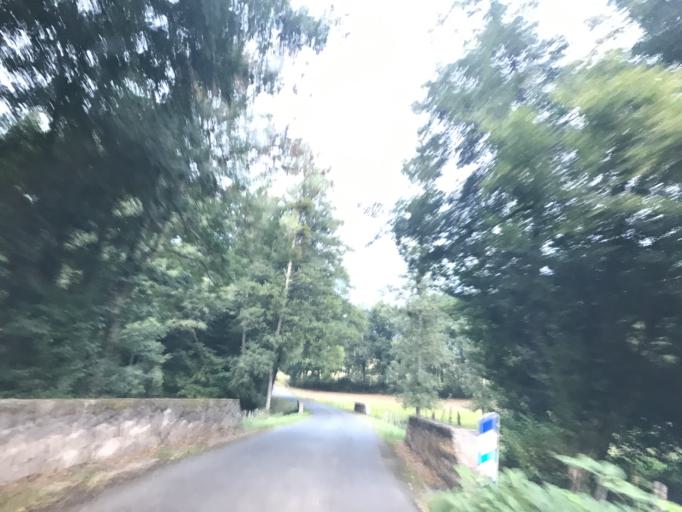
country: FR
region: Auvergne
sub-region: Departement du Puy-de-Dome
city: Escoutoux
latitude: 45.7860
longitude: 3.5850
